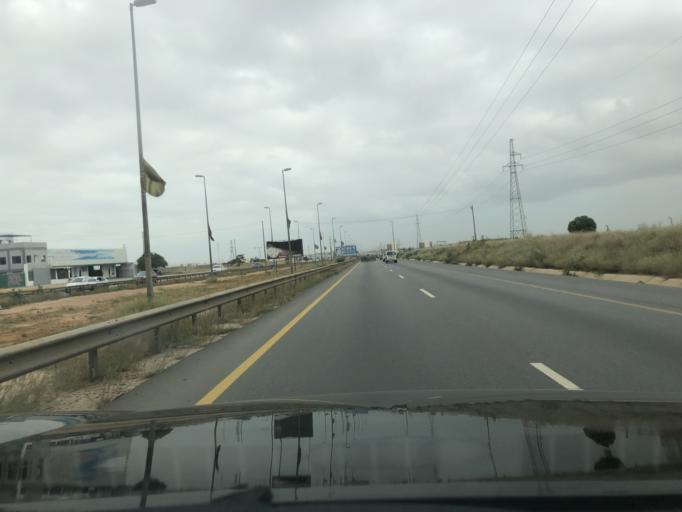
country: AO
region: Luanda
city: Luanda
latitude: -8.9737
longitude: 13.2292
